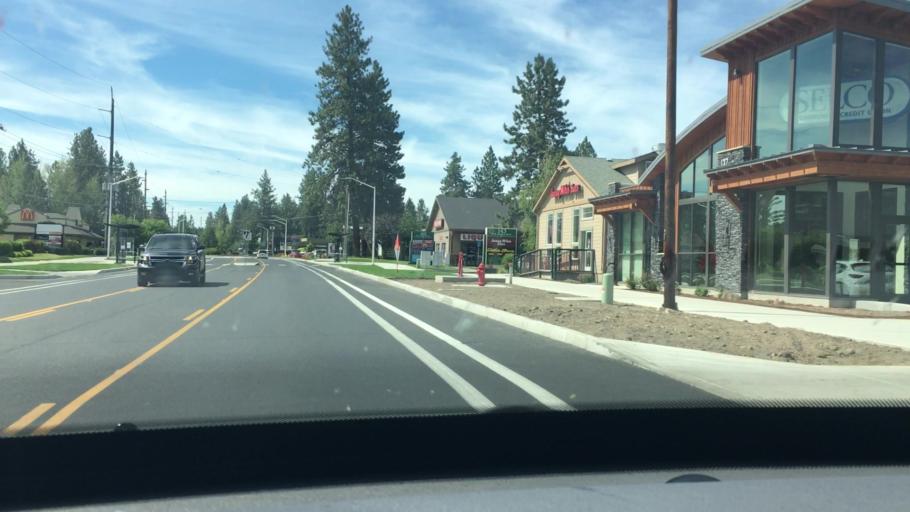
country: US
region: Oregon
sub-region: Deschutes County
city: Bend
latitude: 44.0497
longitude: -121.3319
